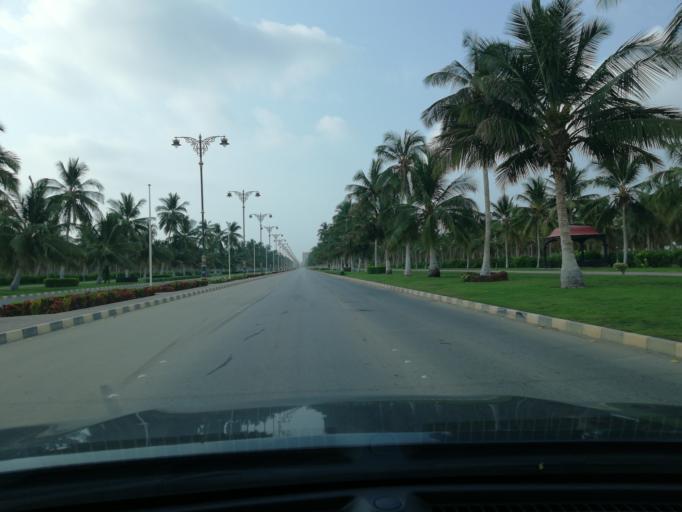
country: OM
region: Zufar
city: Salalah
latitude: 17.0361
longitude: 54.1074
